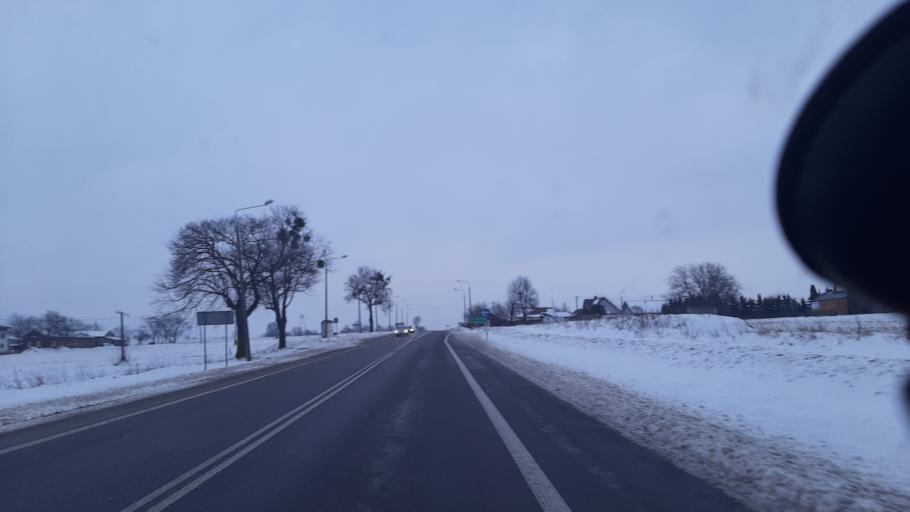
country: PL
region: Lublin Voivodeship
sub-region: Powiat pulawski
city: Markuszow
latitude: 51.3699
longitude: 22.2790
